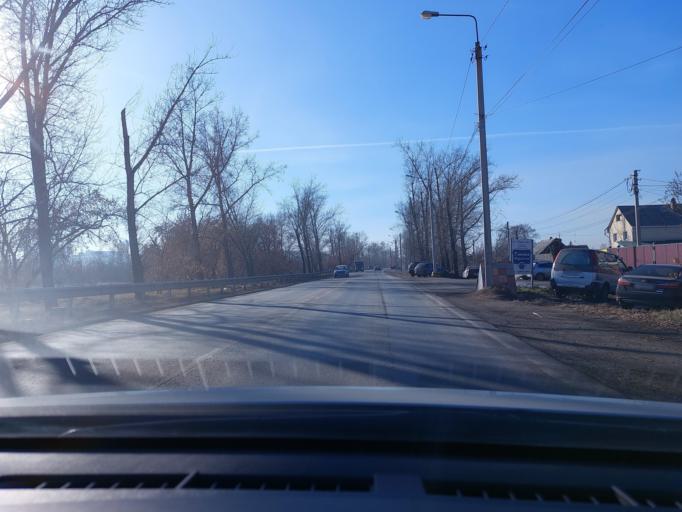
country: RU
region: Irkutsk
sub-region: Irkutskiy Rayon
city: Irkutsk
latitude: 52.3039
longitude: 104.2515
